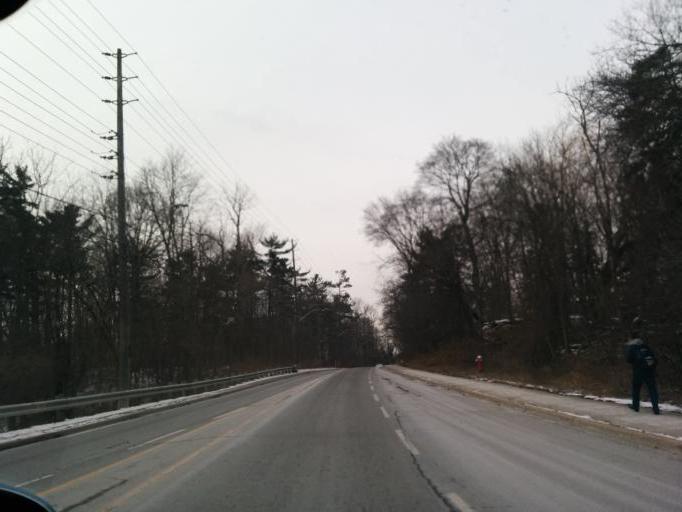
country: CA
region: Ontario
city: Mississauga
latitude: 43.5453
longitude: -79.6634
